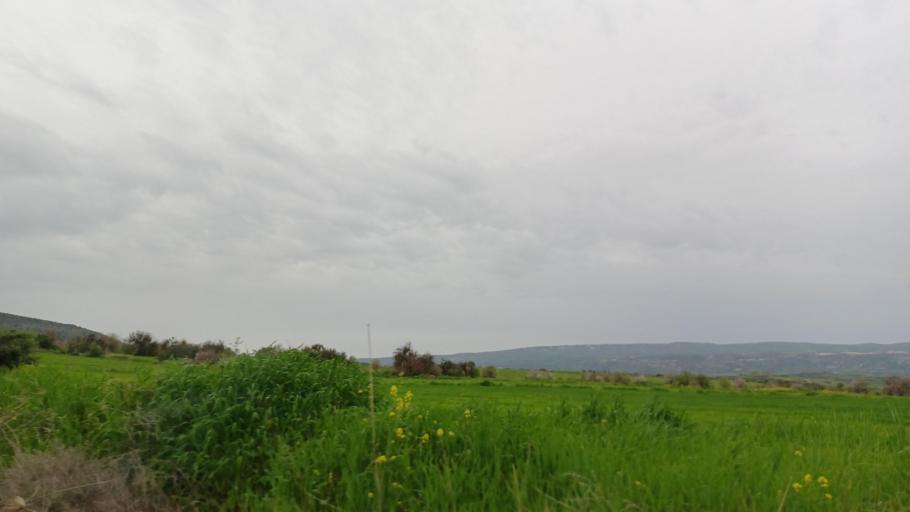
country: CY
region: Pafos
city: Polis
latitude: 35.0464
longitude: 32.4742
